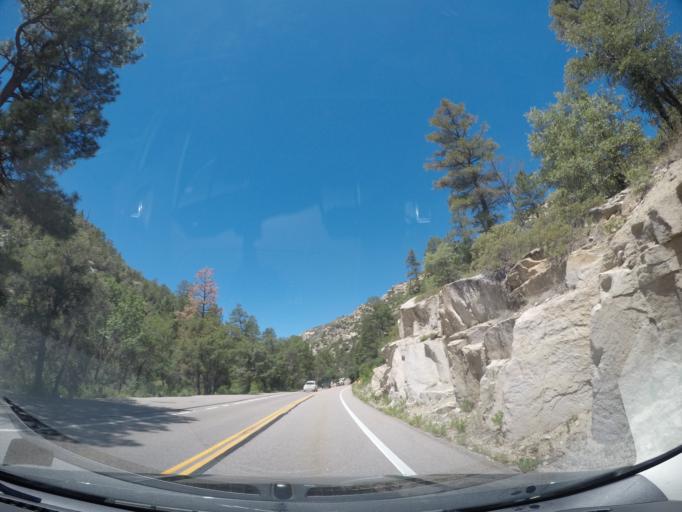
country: US
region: Arizona
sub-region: Pima County
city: Tanque Verde
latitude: 32.3721
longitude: -110.6967
